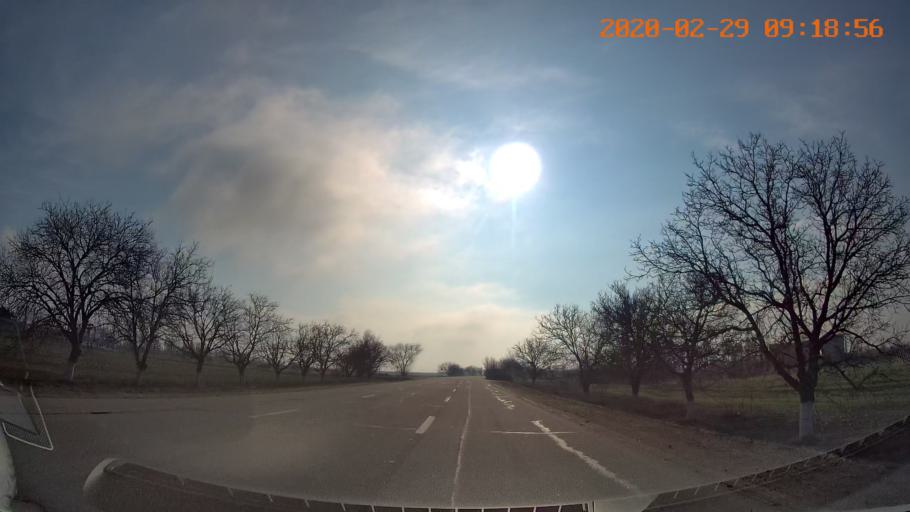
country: MD
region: Telenesti
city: Pervomaisc
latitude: 46.7688
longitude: 29.9323
